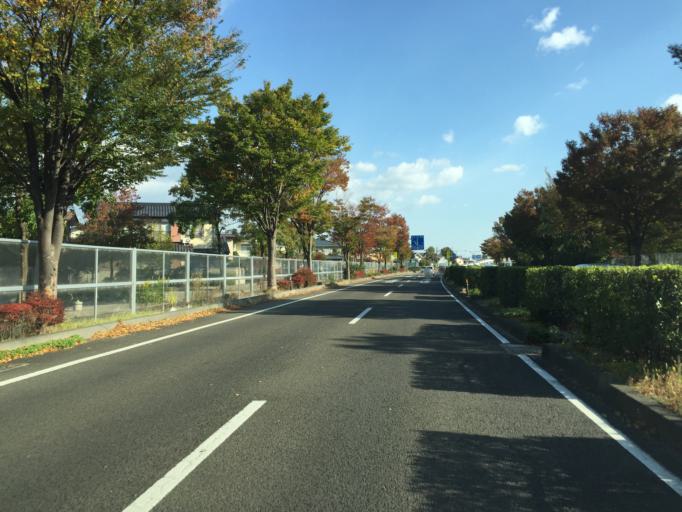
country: JP
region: Fukushima
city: Fukushima-shi
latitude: 37.7738
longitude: 140.4421
